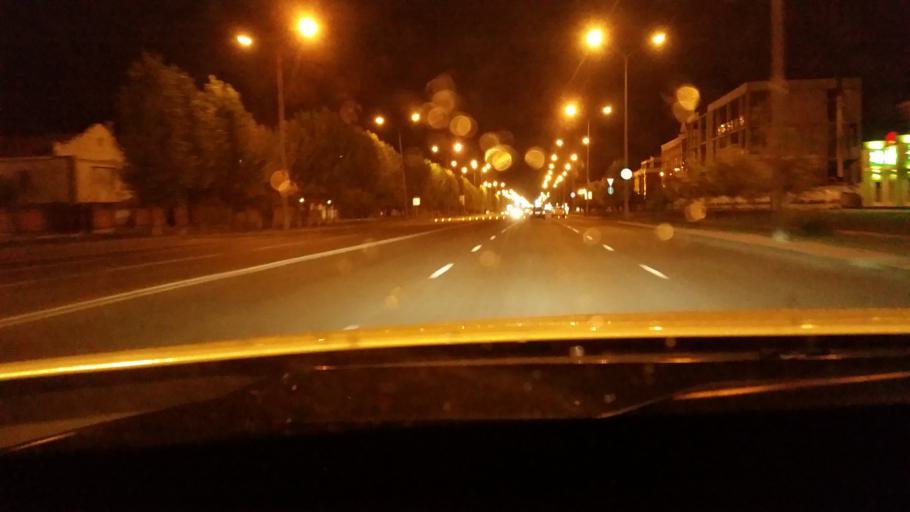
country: KZ
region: Astana Qalasy
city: Astana
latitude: 51.1442
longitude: 71.4865
